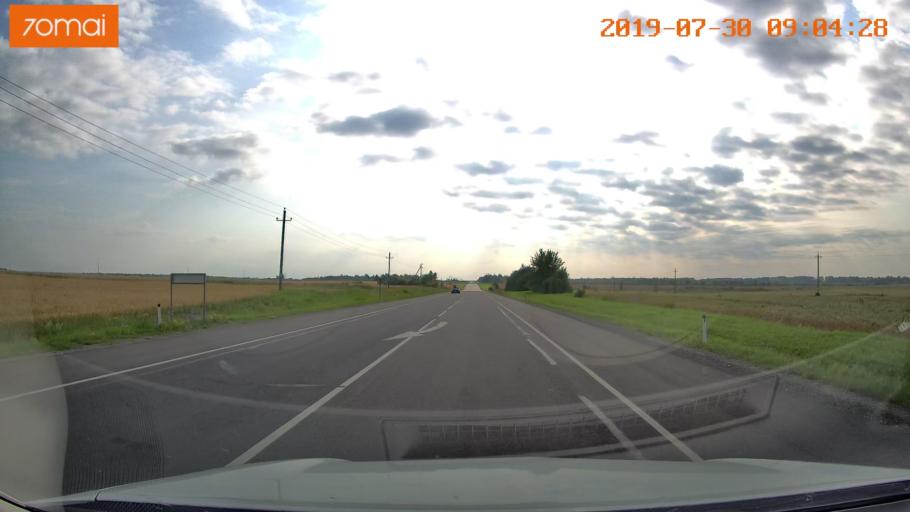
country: RU
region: Kaliningrad
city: Gusev
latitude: 54.6051
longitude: 22.2813
